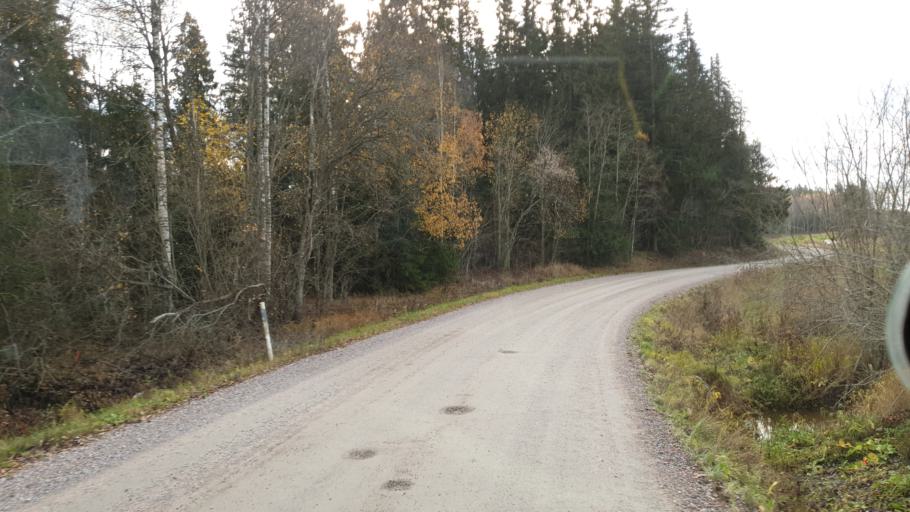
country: FI
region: Uusimaa
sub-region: Helsinki
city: Siuntio
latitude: 60.2313
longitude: 24.3048
